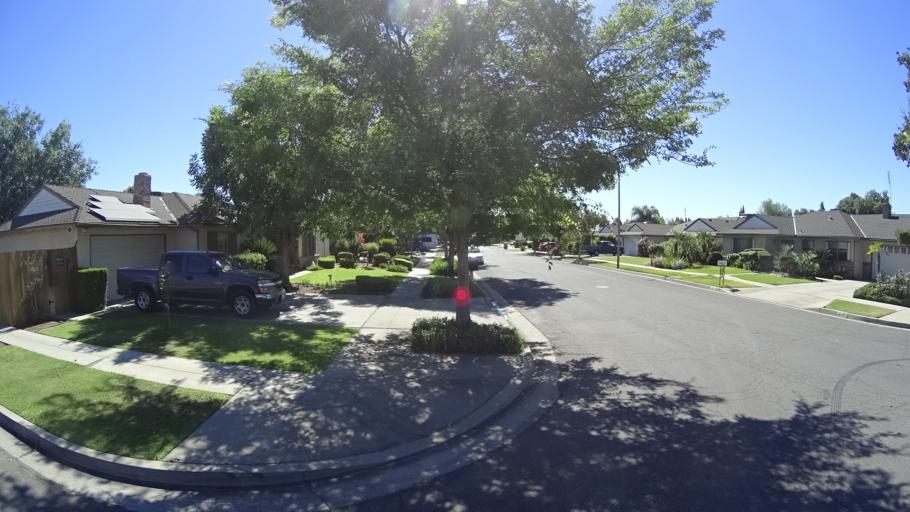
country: US
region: California
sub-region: Fresno County
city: Fresno
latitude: 36.7987
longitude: -119.8332
